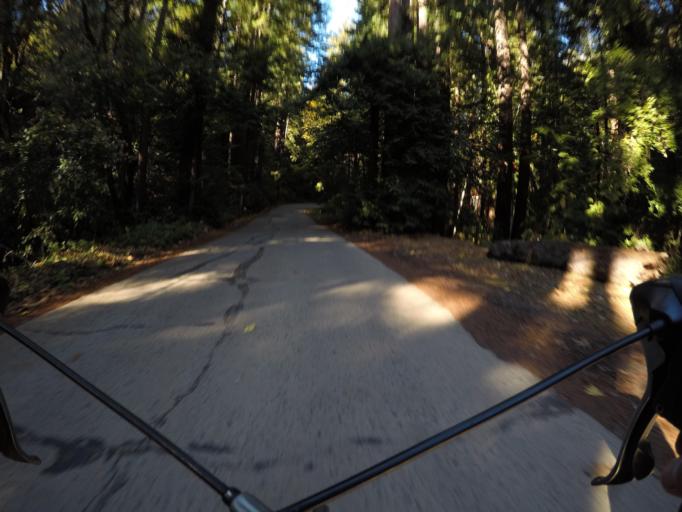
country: US
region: California
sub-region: Santa Clara County
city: Lexington Hills
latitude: 37.1128
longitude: -121.9867
